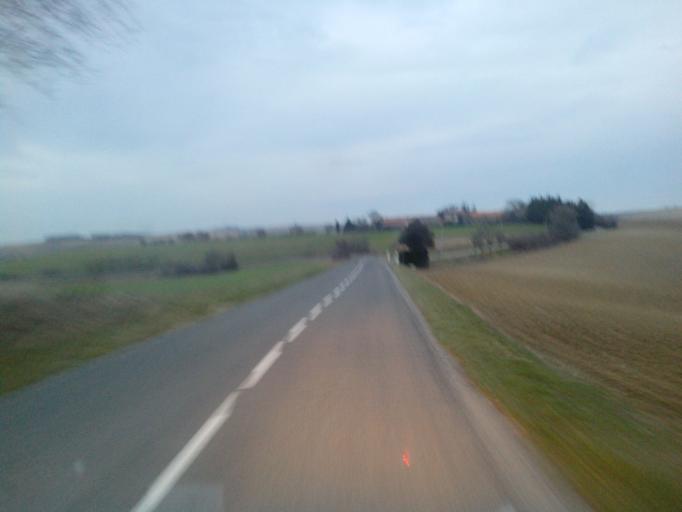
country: FR
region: Languedoc-Roussillon
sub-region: Departement de l'Aude
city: Belpech
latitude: 43.2670
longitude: 1.7488
